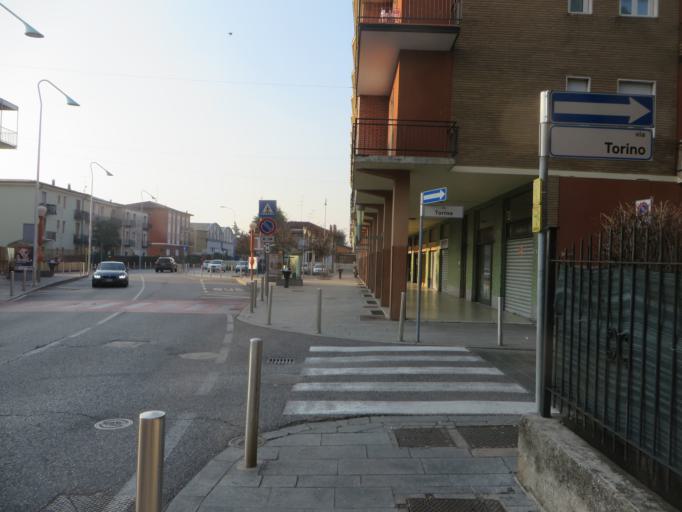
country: IT
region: Lombardy
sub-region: Provincia di Brescia
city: Brescia
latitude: 45.5267
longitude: 10.1895
